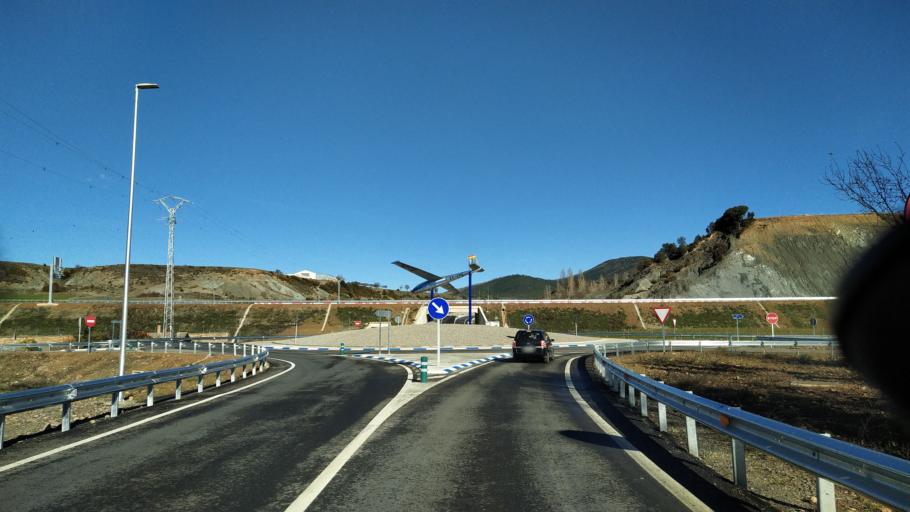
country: ES
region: Aragon
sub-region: Provincia de Huesca
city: Santa Cruz de la Seros
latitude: 42.5636
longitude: -0.7125
